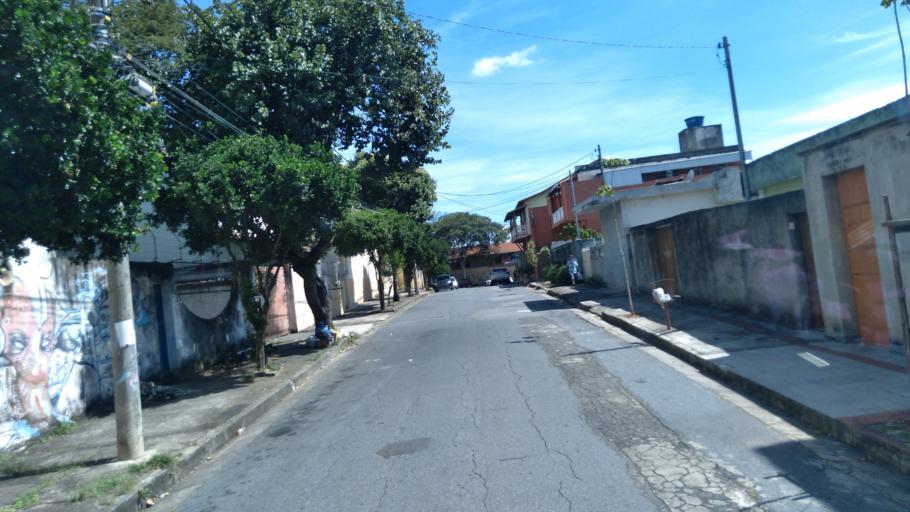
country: BR
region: Minas Gerais
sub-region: Contagem
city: Contagem
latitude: -19.8923
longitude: -44.0149
